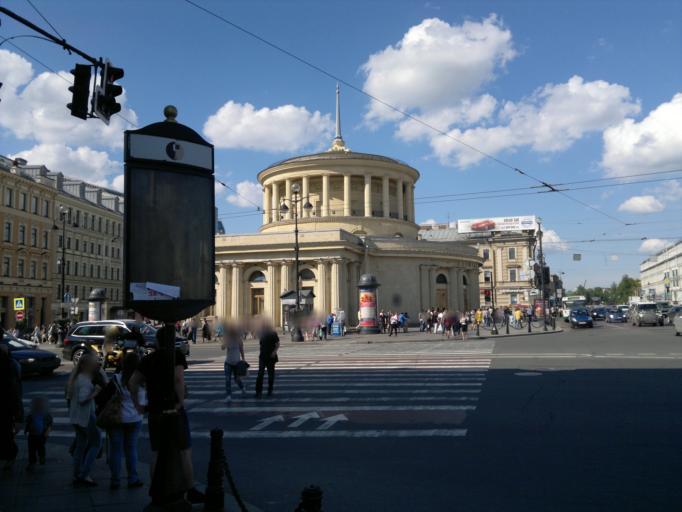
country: RU
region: St.-Petersburg
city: Centralniy
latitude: 59.9309
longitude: 30.3606
